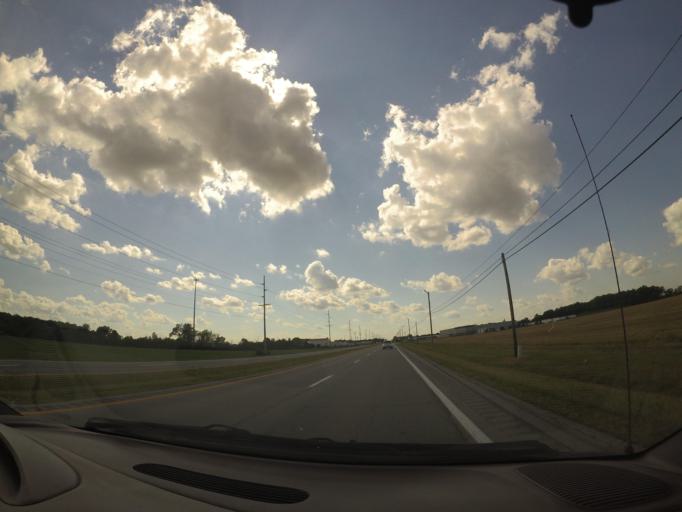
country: US
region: Ohio
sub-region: Sandusky County
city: Clyde
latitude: 41.3026
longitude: -82.9476
